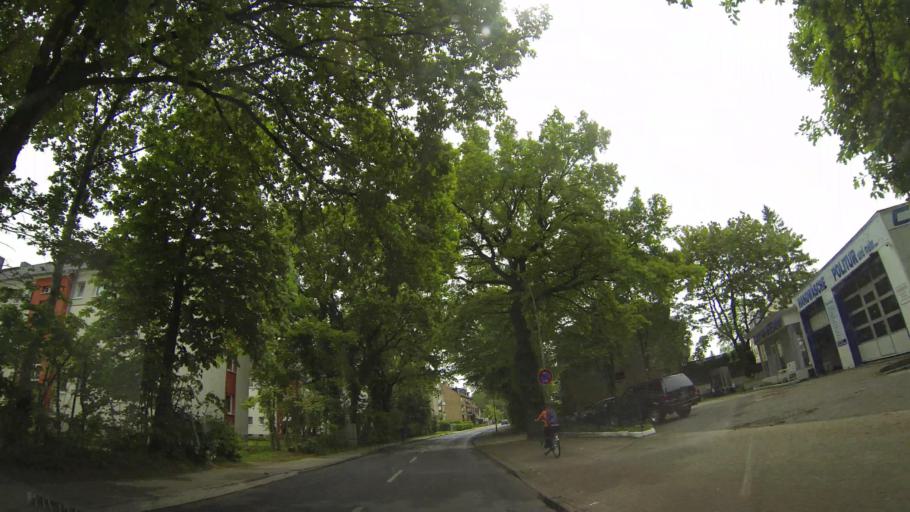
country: DE
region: Schleswig-Holstein
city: Halstenbek
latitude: 53.6022
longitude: 9.8463
